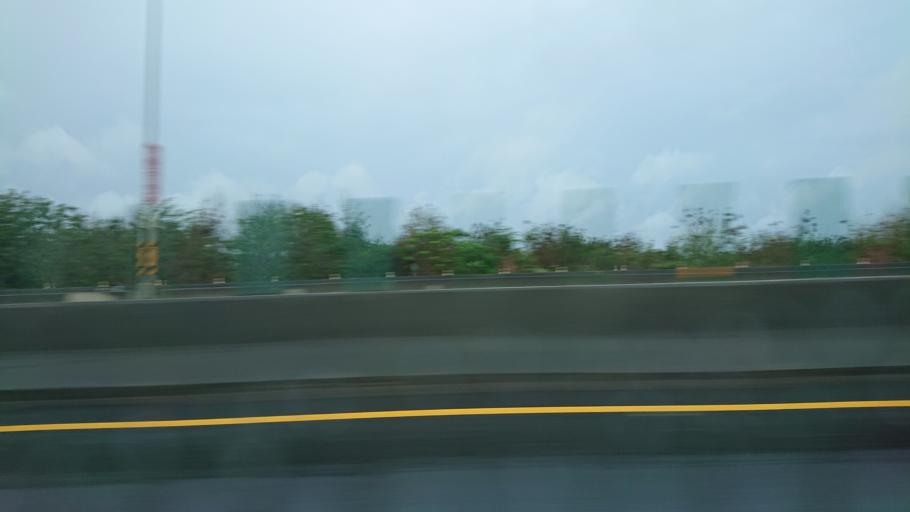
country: TW
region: Taiwan
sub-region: Changhua
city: Chang-hua
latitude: 24.1440
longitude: 120.4483
